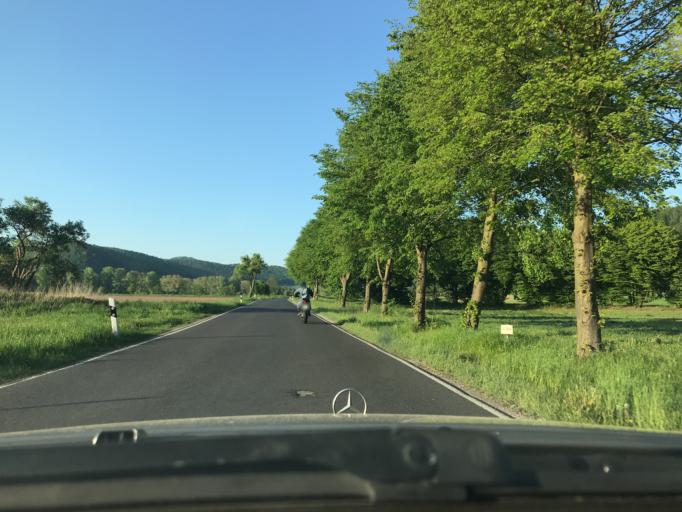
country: DE
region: Hesse
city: Wanfried
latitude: 51.1795
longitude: 10.1311
